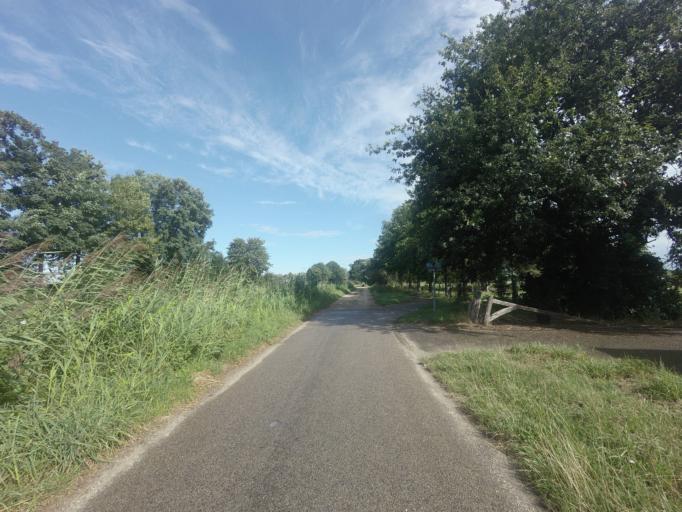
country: NL
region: Overijssel
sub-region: Gemeente Raalte
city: Raalte
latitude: 52.3282
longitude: 6.2647
